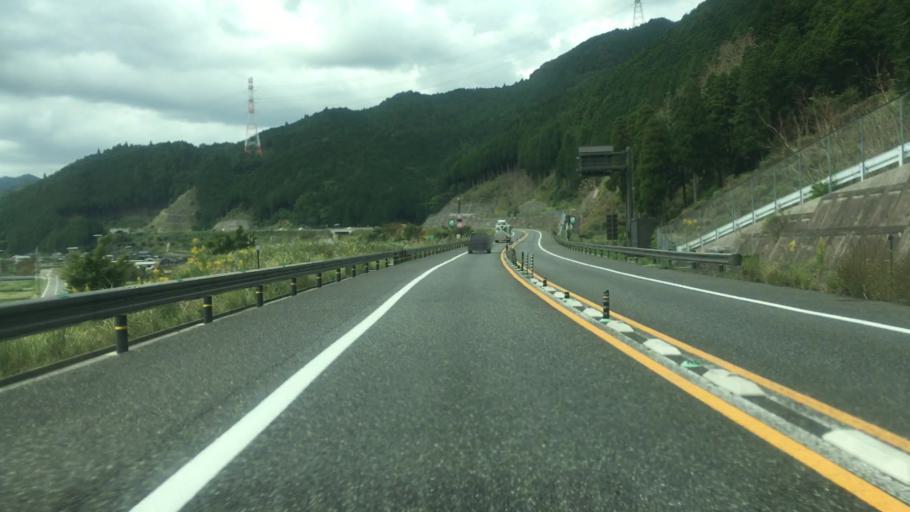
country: JP
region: Kyoto
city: Fukuchiyama
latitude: 35.2806
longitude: 134.9866
